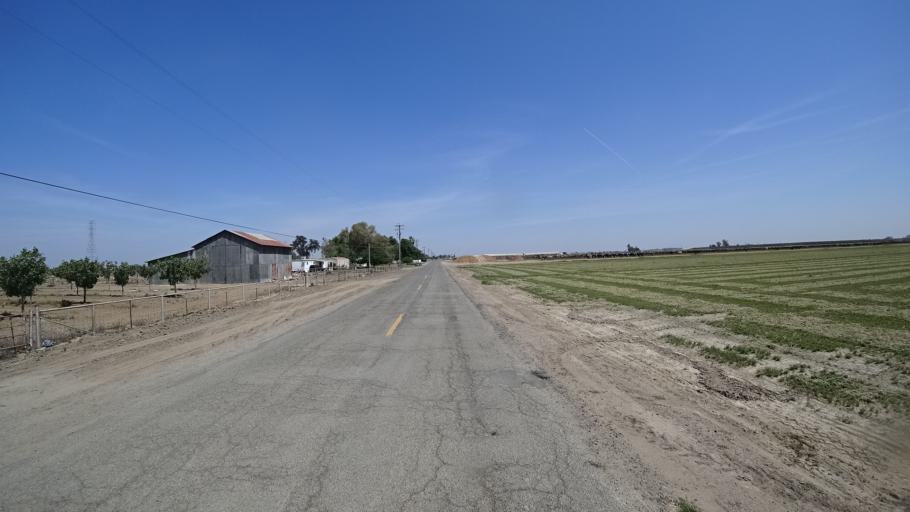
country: US
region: California
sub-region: Fresno County
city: Riverdale
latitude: 36.3923
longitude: -119.8873
